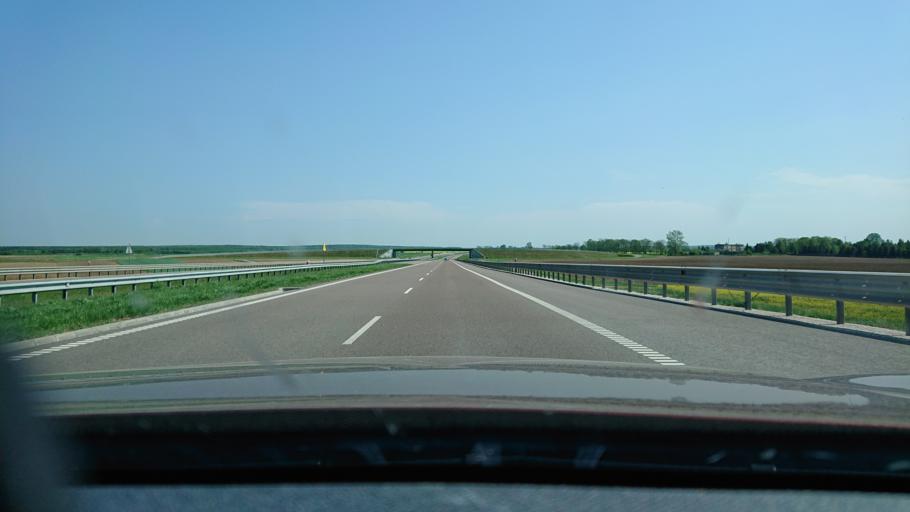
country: PL
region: Subcarpathian Voivodeship
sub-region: Powiat przemyski
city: Stubno
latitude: 49.9341
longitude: 22.9323
